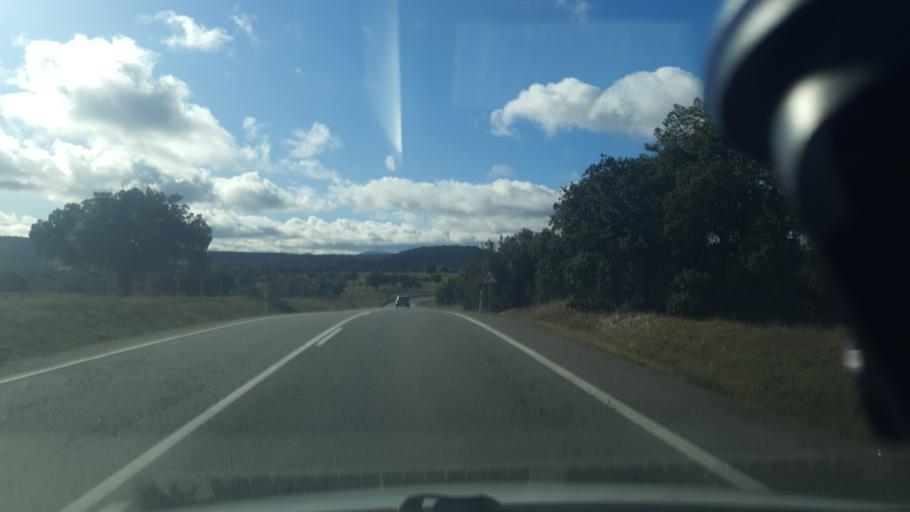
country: ES
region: Castille and Leon
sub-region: Provincia de Segovia
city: Vegas de Matute
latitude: 40.8105
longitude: -4.3036
